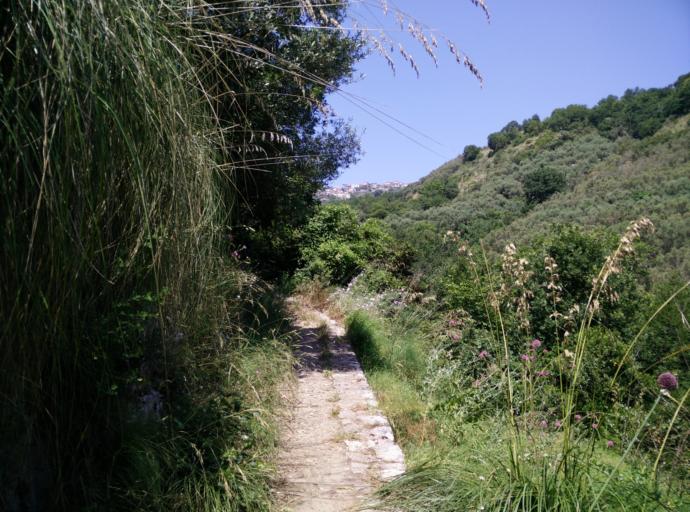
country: IT
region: Campania
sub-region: Provincia di Napoli
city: Massa Lubrense
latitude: 40.5959
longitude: 14.3805
